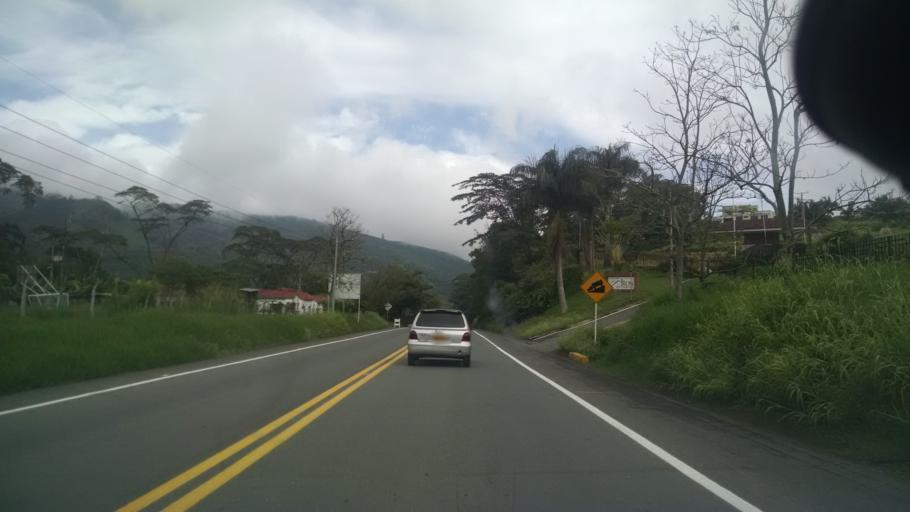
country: CO
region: Caldas
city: Palestina
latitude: 5.0270
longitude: -75.5970
